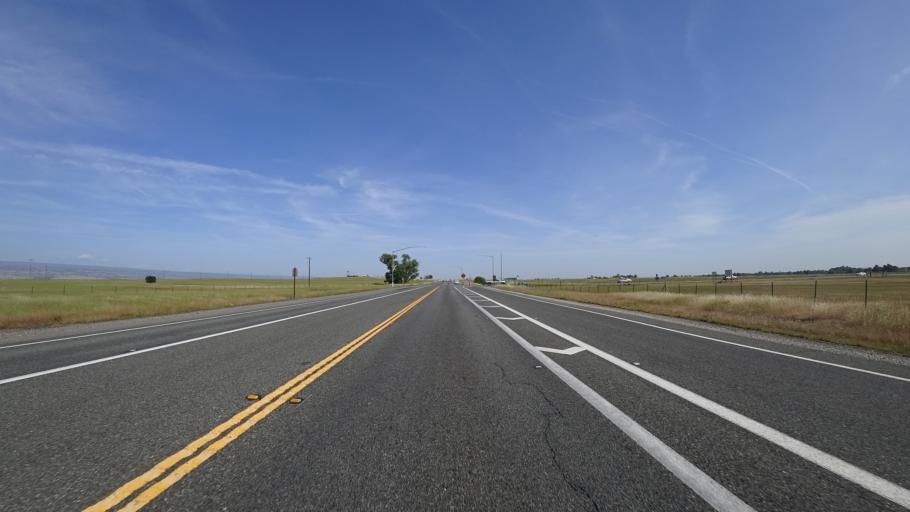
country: US
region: California
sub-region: Tehama County
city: Los Molinos
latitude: 39.9327
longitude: -122.0342
